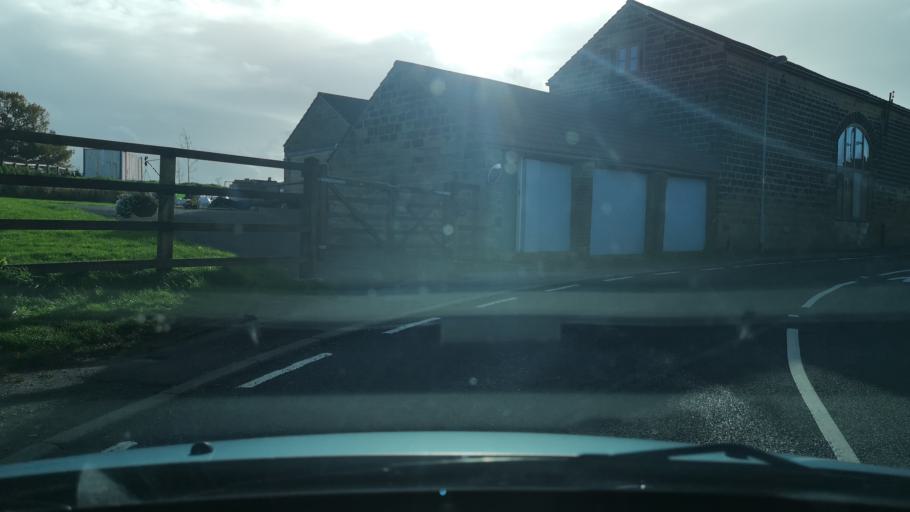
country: GB
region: England
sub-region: City and Borough of Wakefield
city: Ryhill
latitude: 53.6379
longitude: -1.4197
